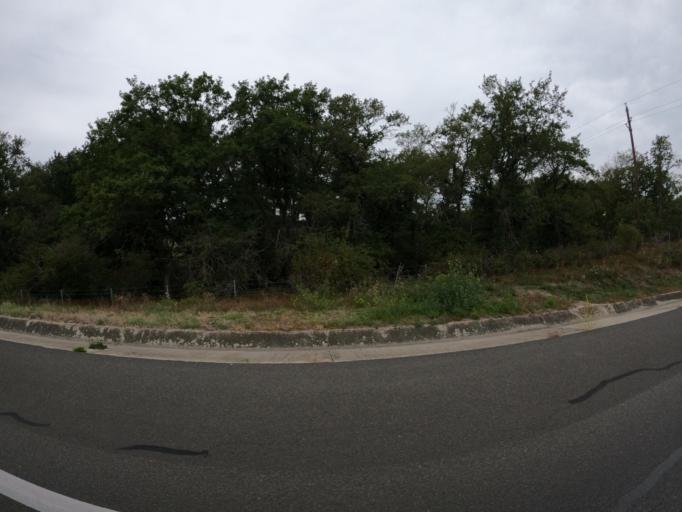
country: FR
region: Auvergne
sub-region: Departement de l'Allier
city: Domerat
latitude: 46.3401
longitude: 2.5368
